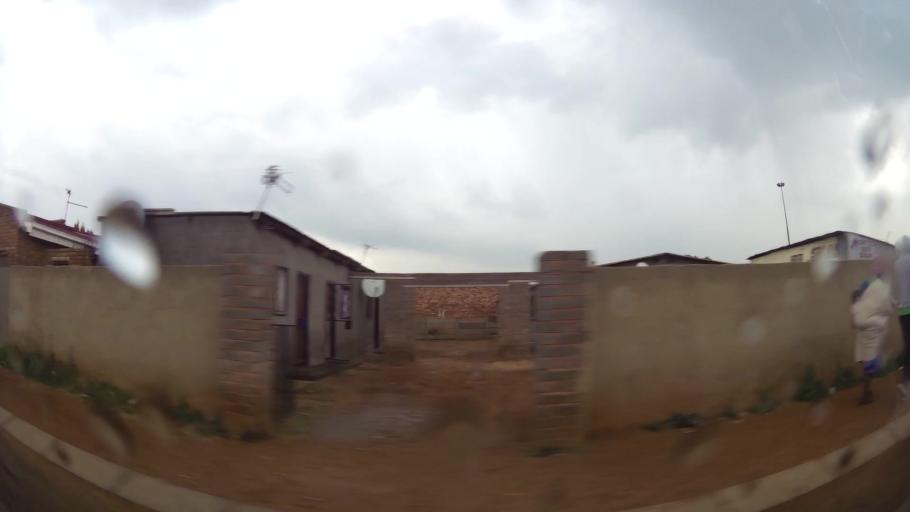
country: ZA
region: Gauteng
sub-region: Ekurhuleni Metropolitan Municipality
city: Germiston
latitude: -26.3627
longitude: 28.1649
